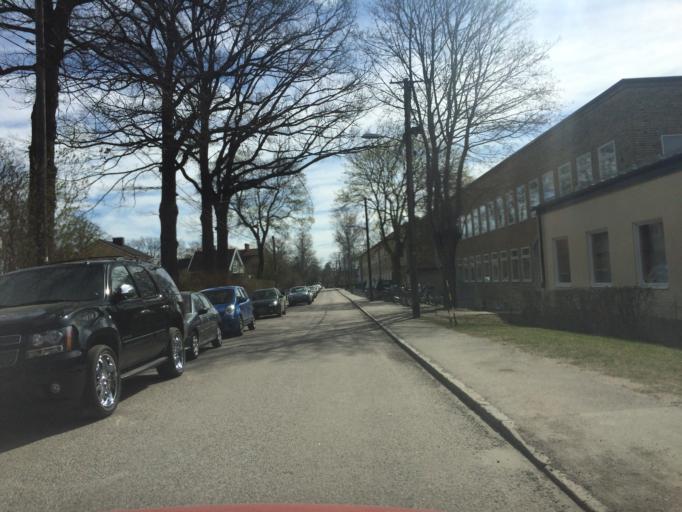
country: SE
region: Stockholm
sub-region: Huddinge Kommun
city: Huddinge
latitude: 59.2783
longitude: 17.9817
